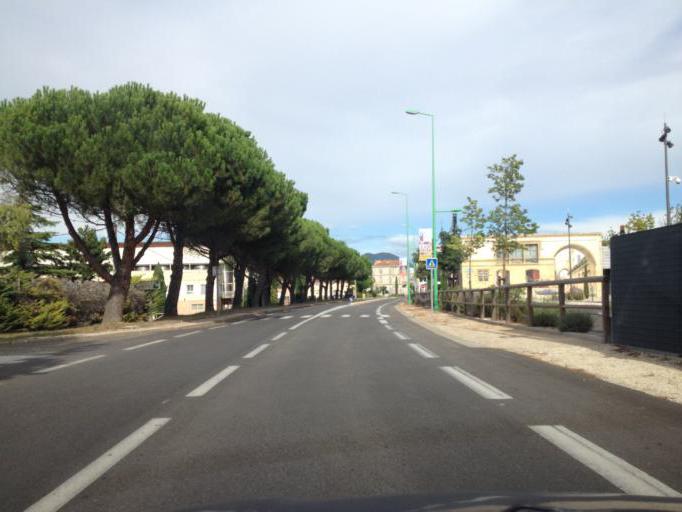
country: FR
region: Provence-Alpes-Cote d'Azur
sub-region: Departement du Vaucluse
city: Valreas
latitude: 44.3874
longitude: 4.9875
